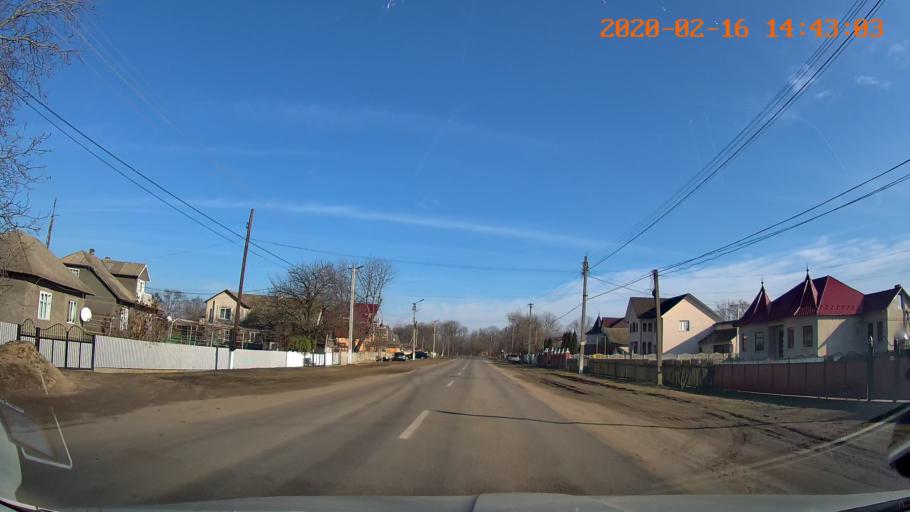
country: RO
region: Botosani
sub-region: Comuna Paltinis
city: Paltinis
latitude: 48.2581
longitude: 26.5932
